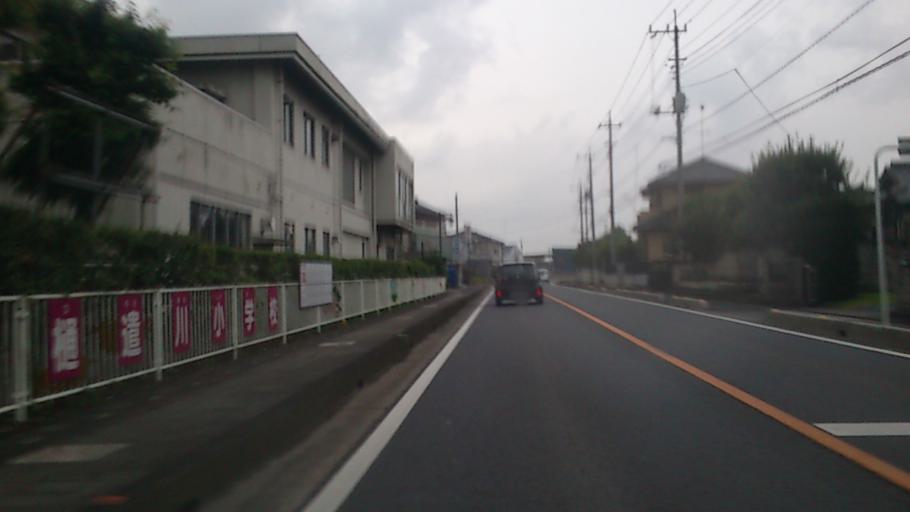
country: JP
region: Saitama
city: Kazo
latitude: 36.1552
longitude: 139.6195
